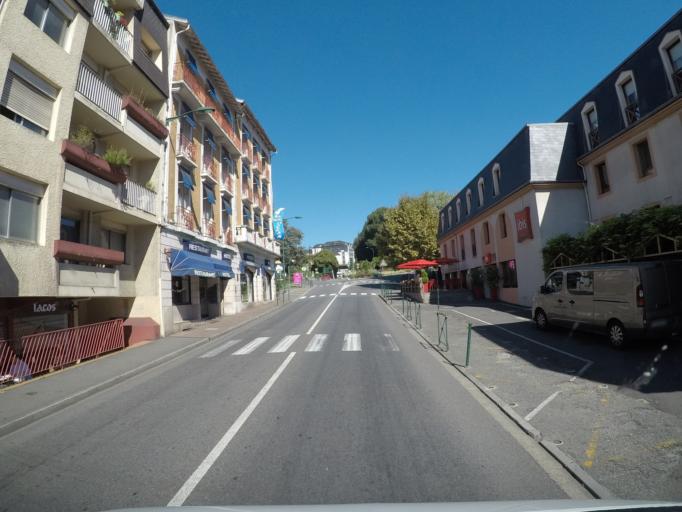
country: FR
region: Midi-Pyrenees
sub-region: Departement des Hautes-Pyrenees
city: Lourdes
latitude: 43.0986
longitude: -0.0455
